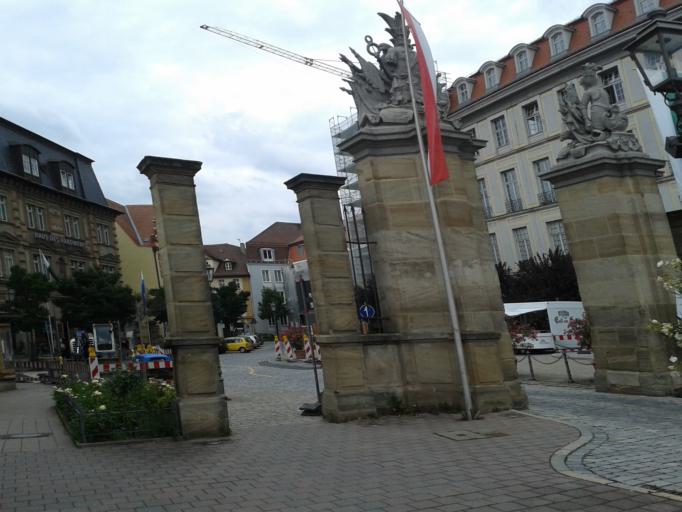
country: DE
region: Bavaria
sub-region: Regierungsbezirk Mittelfranken
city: Ansbach
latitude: 49.3018
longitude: 10.5760
